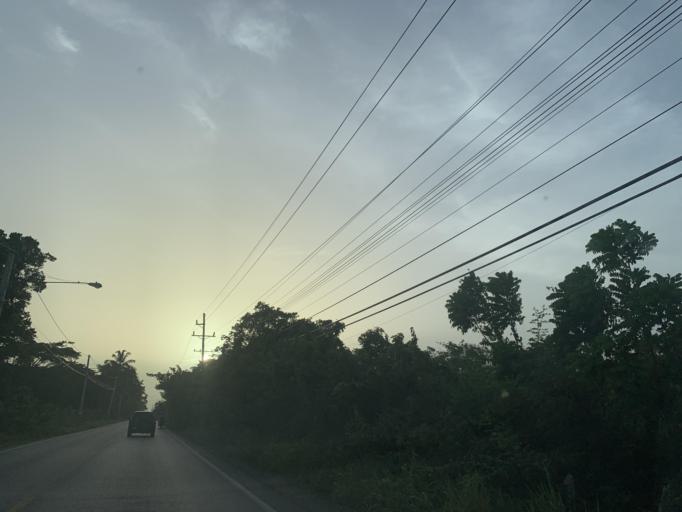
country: DO
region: Puerto Plata
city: Cabarete
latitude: 19.7748
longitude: -70.4642
